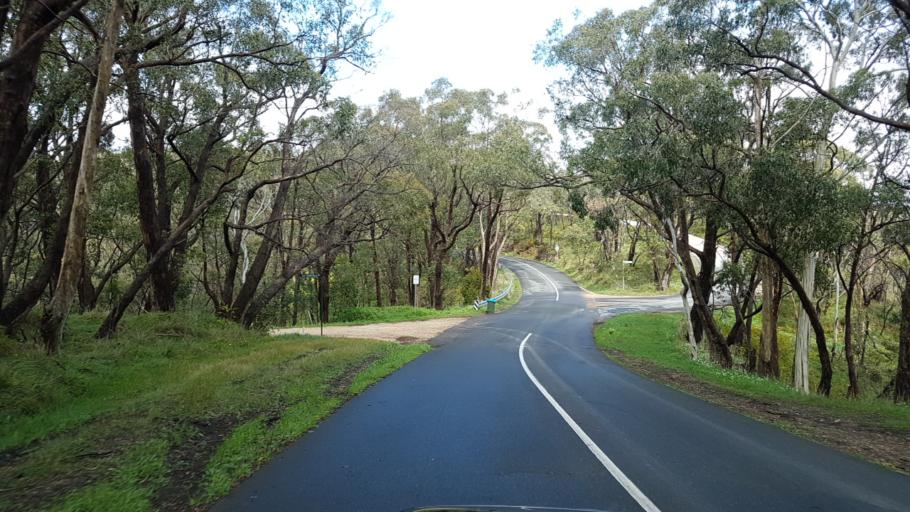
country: AU
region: South Australia
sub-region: Adelaide Hills
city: Adelaide Hills
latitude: -34.9104
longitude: 138.7587
